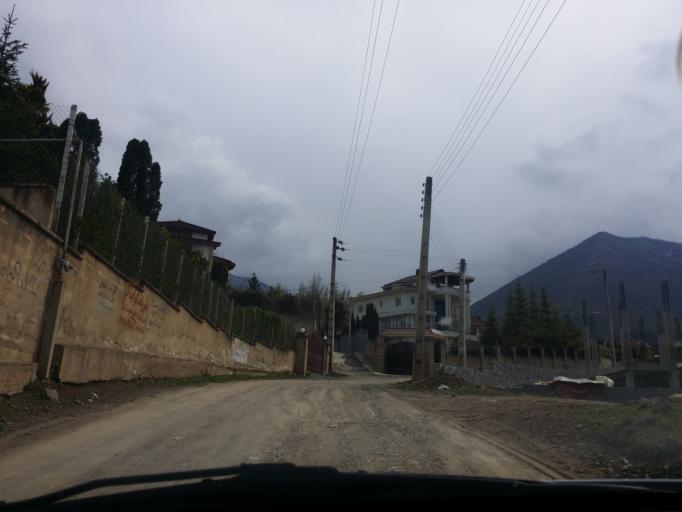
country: IR
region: Mazandaran
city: `Abbasabad
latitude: 36.4881
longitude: 51.1419
